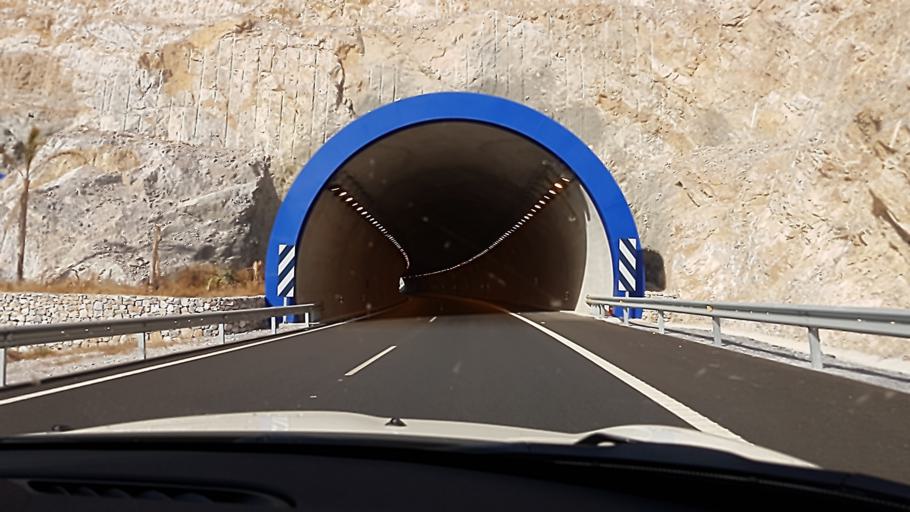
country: ES
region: Andalusia
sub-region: Provincia de Granada
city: Gualchos
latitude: 36.7201
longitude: -3.3765
